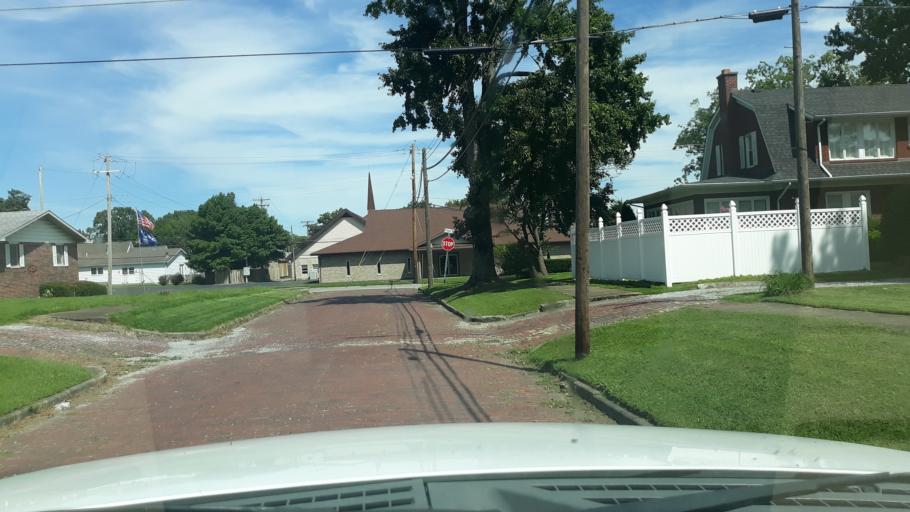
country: US
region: Illinois
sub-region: Saline County
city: Eldorado
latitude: 37.8130
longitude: -88.4427
